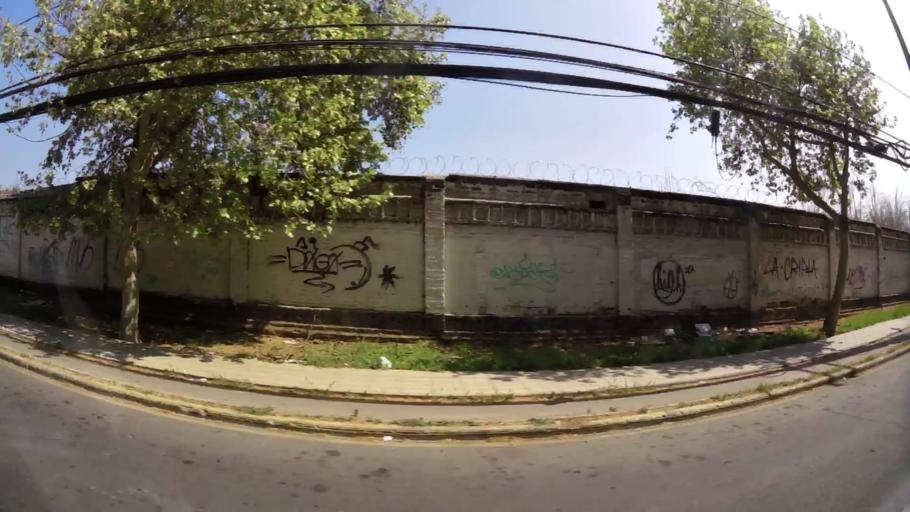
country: CL
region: Santiago Metropolitan
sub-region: Provincia de Santiago
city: Santiago
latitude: -33.4685
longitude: -70.6650
